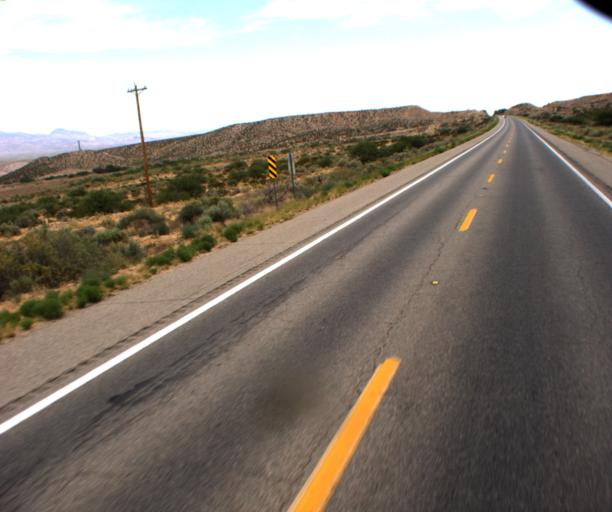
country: US
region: Arizona
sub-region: Graham County
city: Bylas
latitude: 33.0827
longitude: -110.0481
